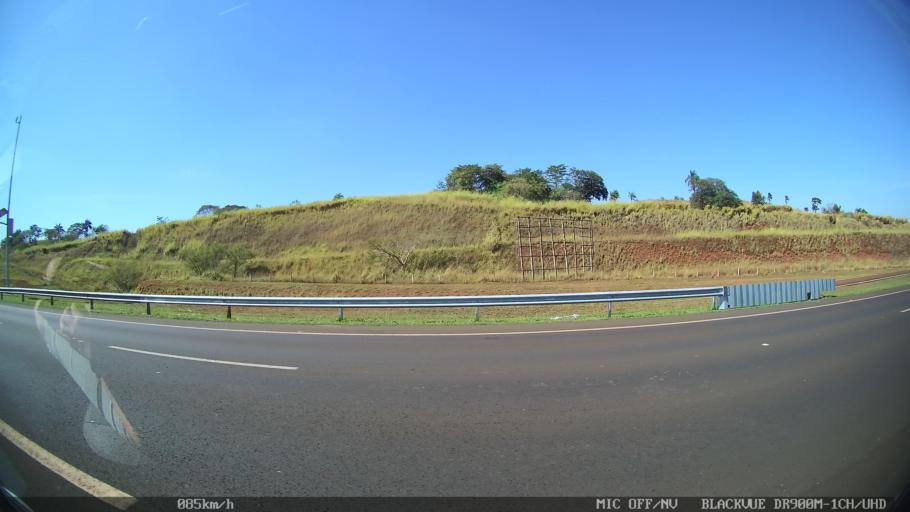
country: BR
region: Sao Paulo
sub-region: Franca
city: Franca
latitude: -20.6104
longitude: -47.4544
